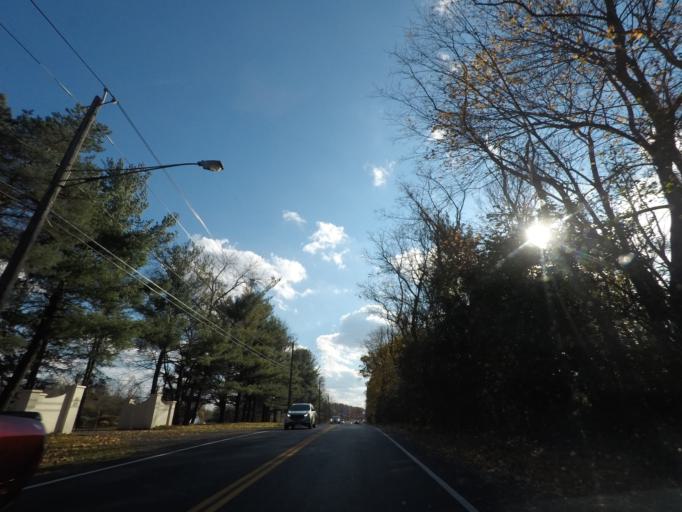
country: US
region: New York
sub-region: Schenectady County
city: Niskayuna
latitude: 42.7870
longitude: -73.8931
